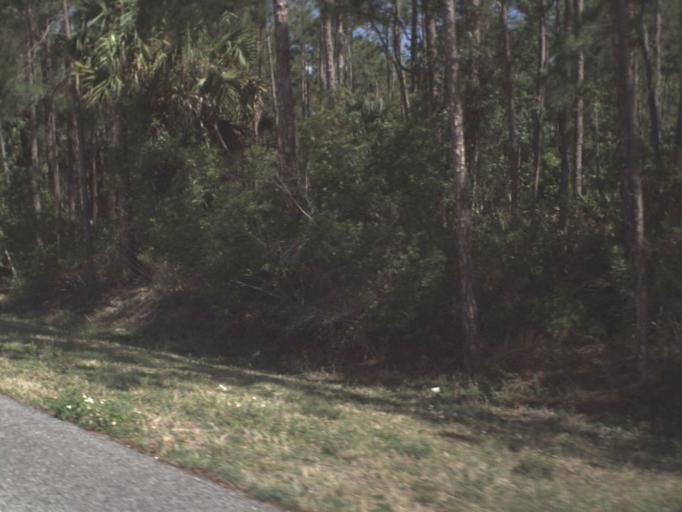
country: US
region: Florida
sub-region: Volusia County
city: Ormond-by-the-Sea
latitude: 29.3608
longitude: -81.1646
